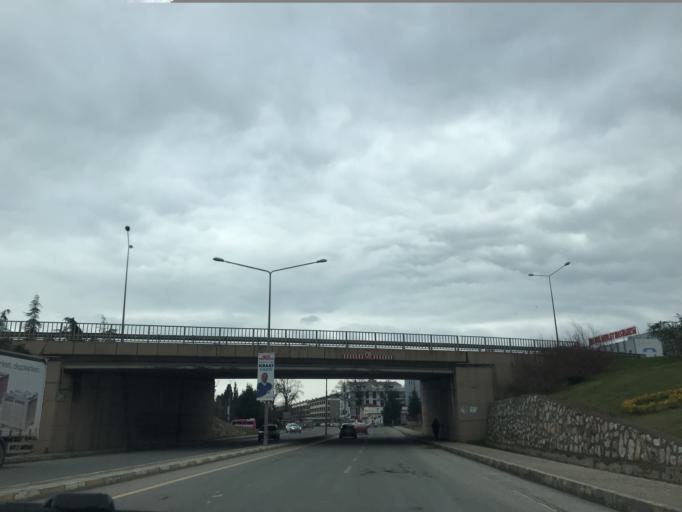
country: TR
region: Yalova
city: Ciftlikkoy
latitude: 40.6613
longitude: 29.3065
